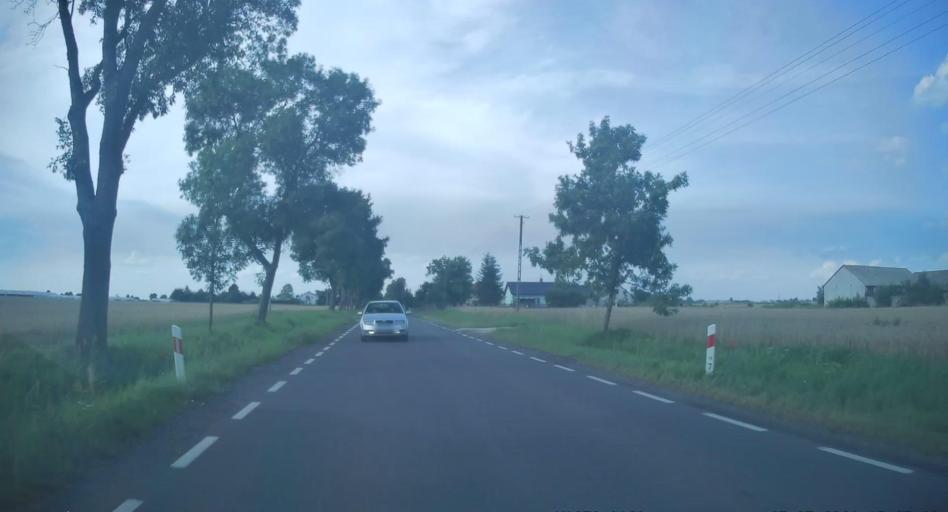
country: PL
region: Lodz Voivodeship
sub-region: Powiat tomaszowski
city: Rzeczyca
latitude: 51.6031
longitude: 20.2937
